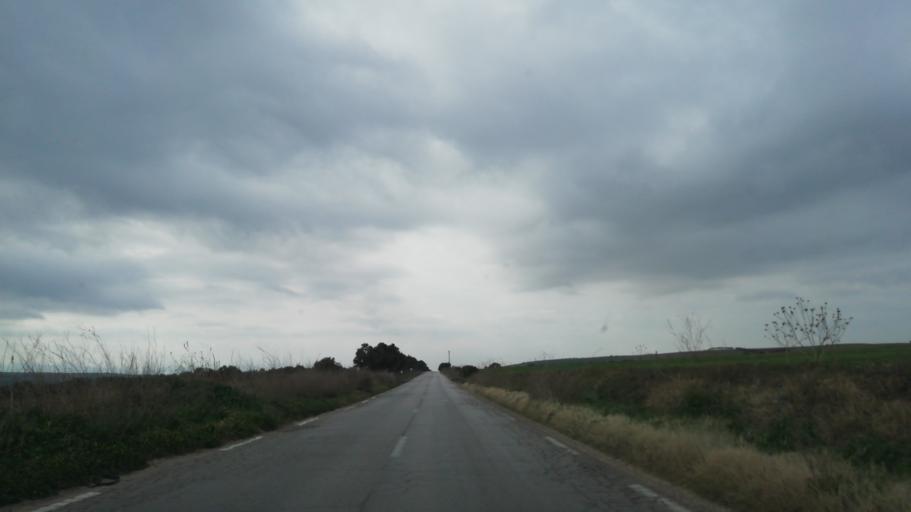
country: DZ
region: Oran
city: Sidi ech Chahmi
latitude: 35.6182
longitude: -0.4158
